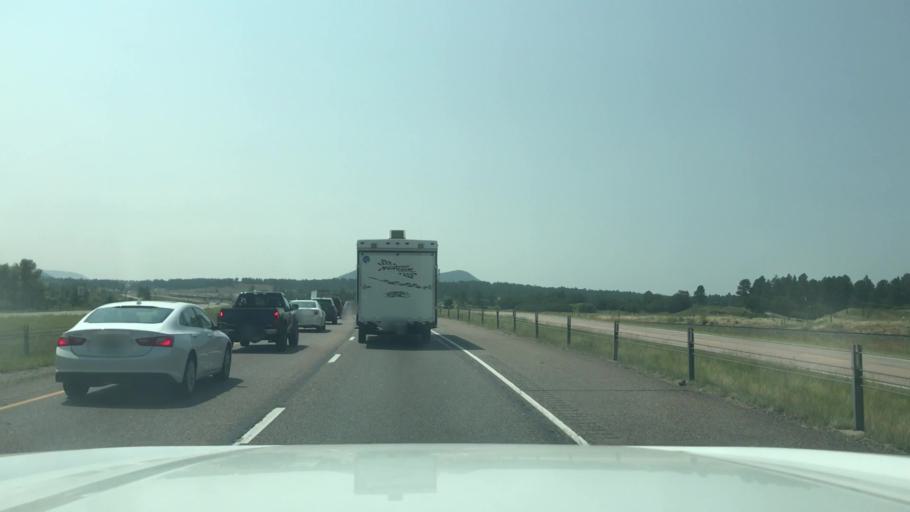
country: US
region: Colorado
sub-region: Douglas County
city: Perry Park
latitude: 39.2769
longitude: -104.8975
